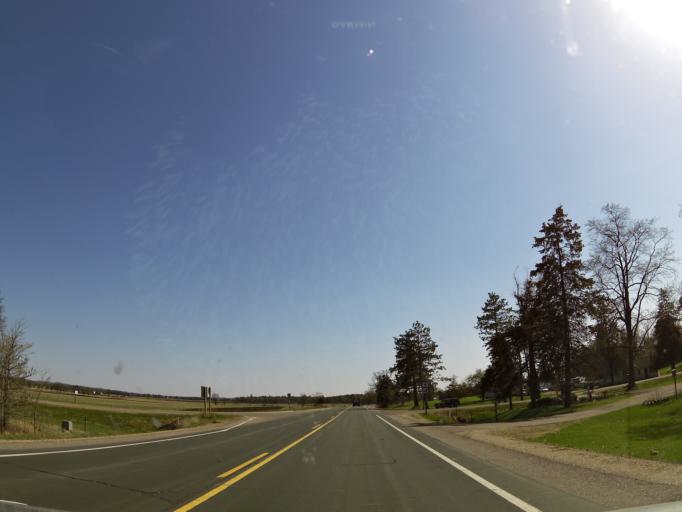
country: US
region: Wisconsin
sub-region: Pepin County
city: Durand
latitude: 44.7208
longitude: -91.9333
